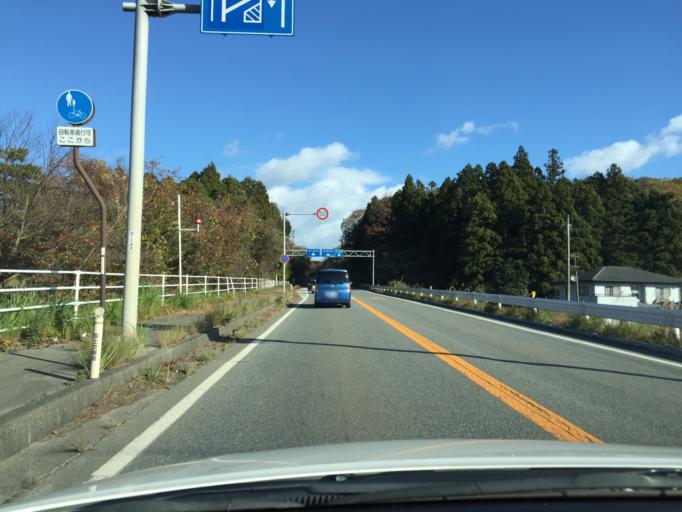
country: JP
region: Fukushima
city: Namie
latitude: 37.2904
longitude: 140.9923
